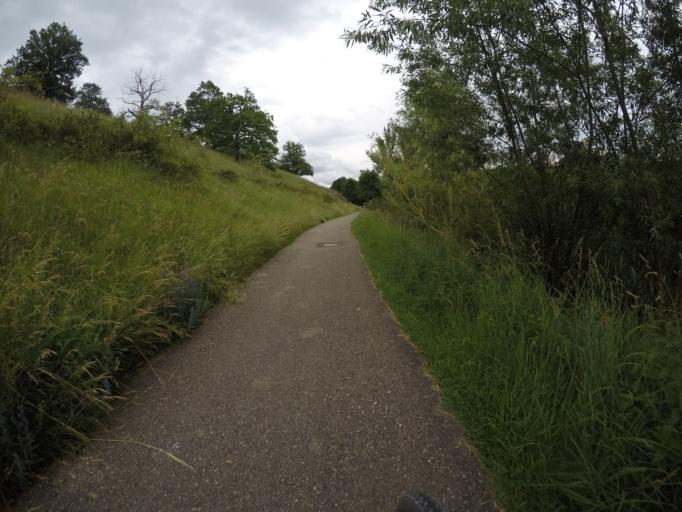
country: DE
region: Baden-Wuerttemberg
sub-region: Tuebingen Region
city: Westerstetten
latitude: 48.5191
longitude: 9.9612
